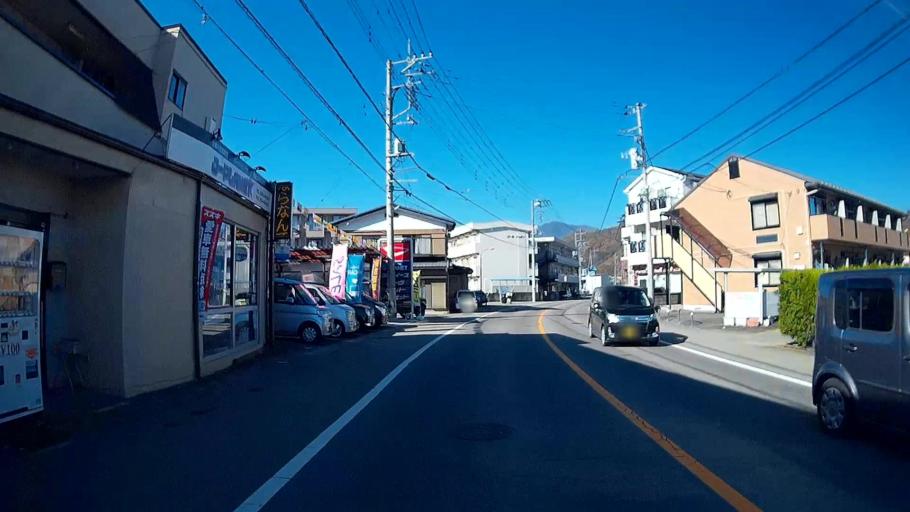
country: JP
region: Yamanashi
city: Otsuki
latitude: 35.5405
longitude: 138.8957
